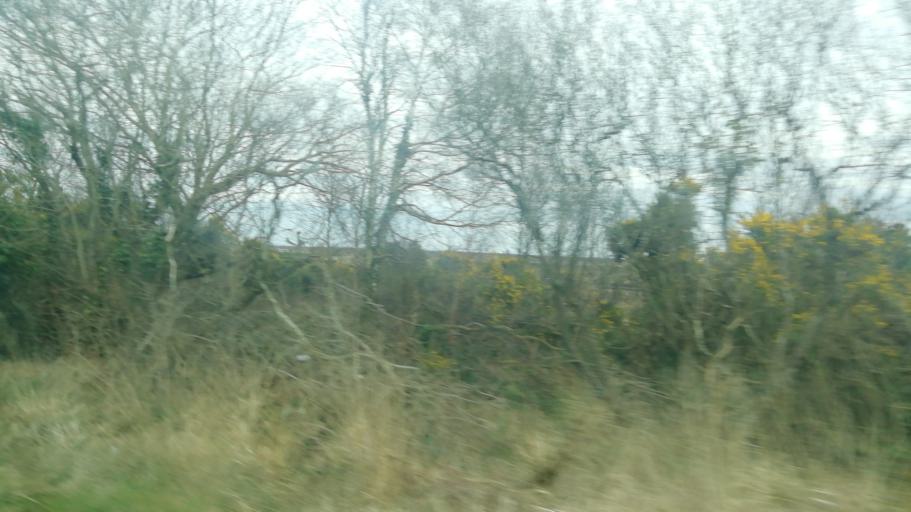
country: IE
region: Leinster
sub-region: Kildare
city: Rathangan
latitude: 53.2551
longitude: -7.0132
